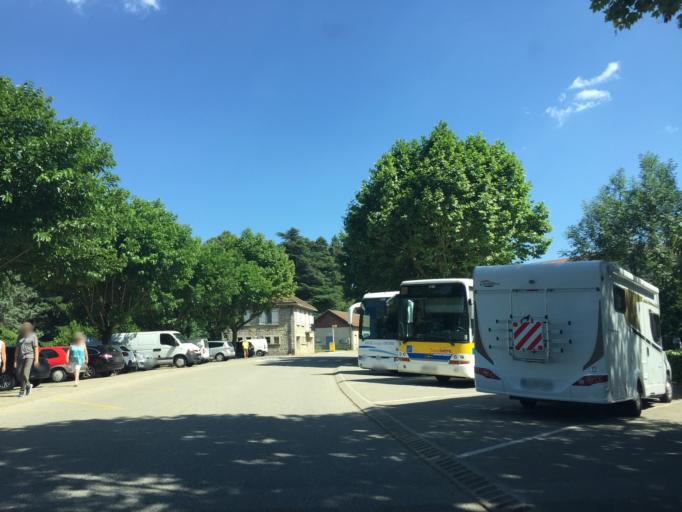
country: FR
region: Rhone-Alpes
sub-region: Departement de l'Isere
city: Saint-Hilaire-du-Rosier
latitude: 45.0601
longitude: 5.2489
